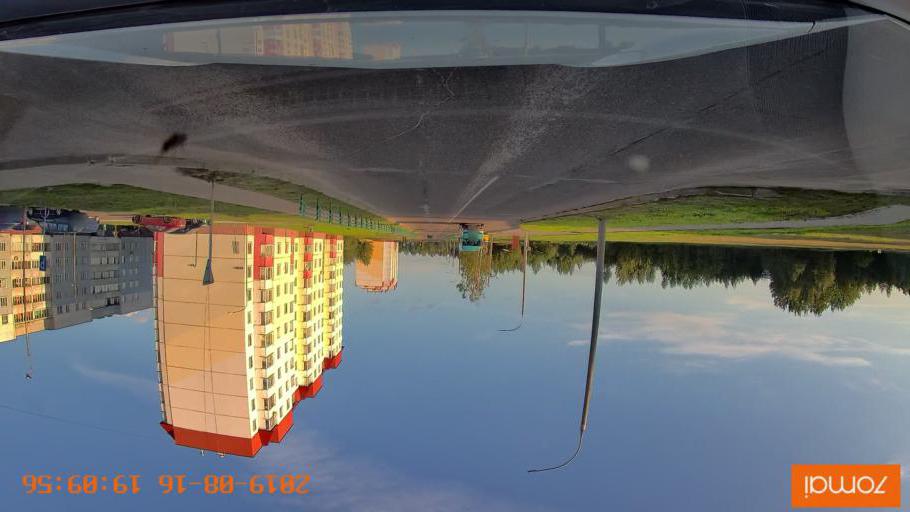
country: BY
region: Mogilev
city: Asipovichy
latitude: 53.3212
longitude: 28.6372
